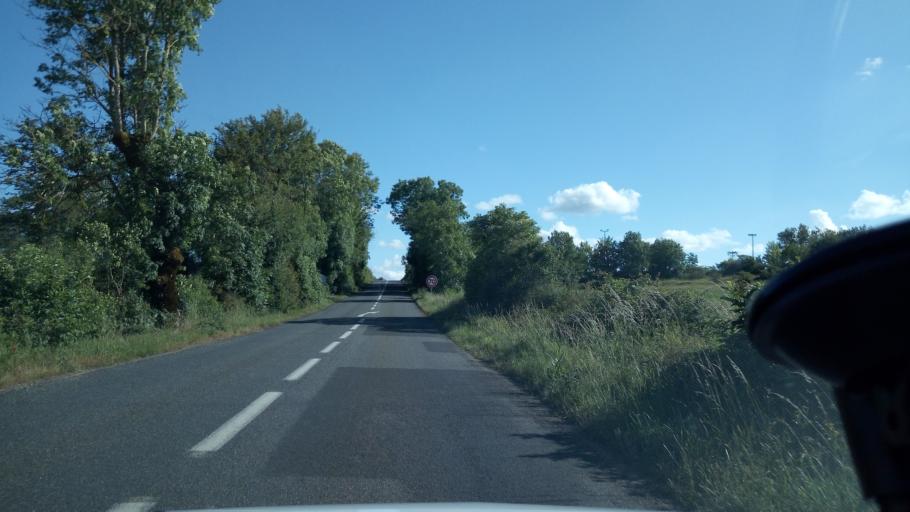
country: FR
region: Midi-Pyrenees
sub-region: Departement de l'Aveyron
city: Sebazac-Concoures
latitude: 44.4138
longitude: 2.6062
